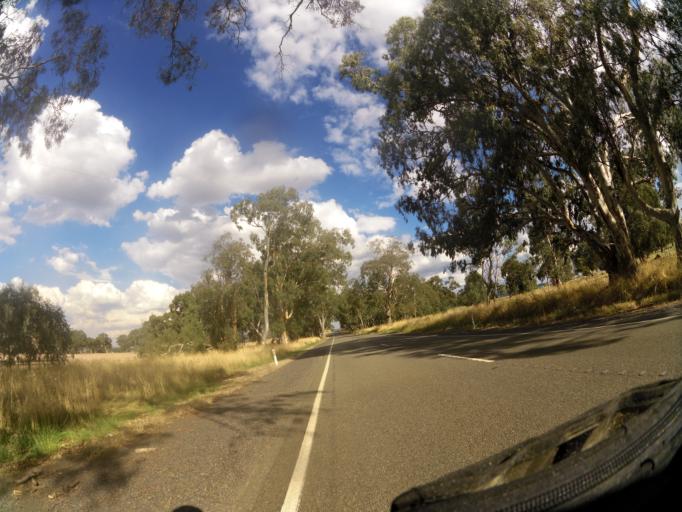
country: AU
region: Victoria
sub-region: Mansfield
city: Mansfield
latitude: -37.0123
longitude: 146.0859
